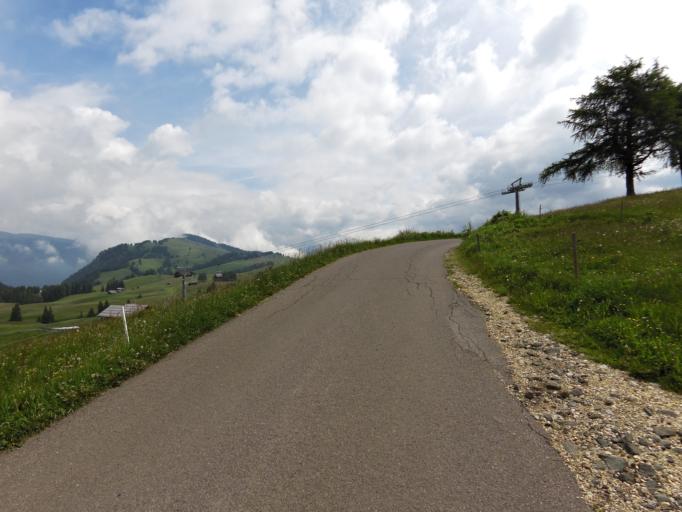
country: IT
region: Trentino-Alto Adige
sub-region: Bolzano
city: Ortisei
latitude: 46.5384
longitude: 11.6226
